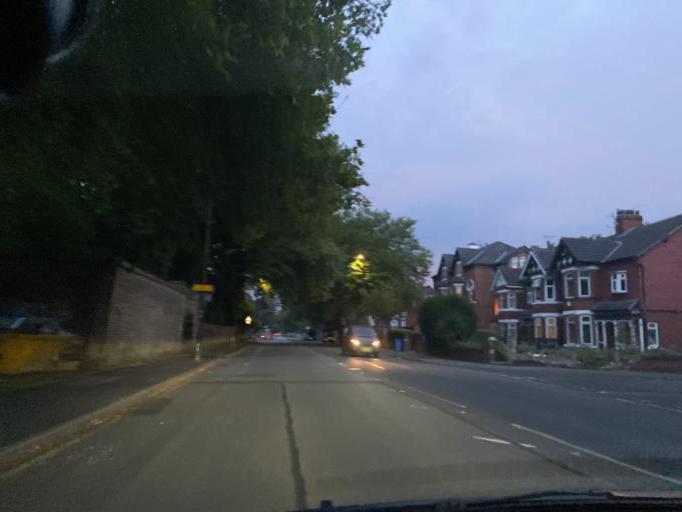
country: GB
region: England
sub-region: Manchester
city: Chorlton cum Hardy
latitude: 53.4527
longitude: -2.2682
